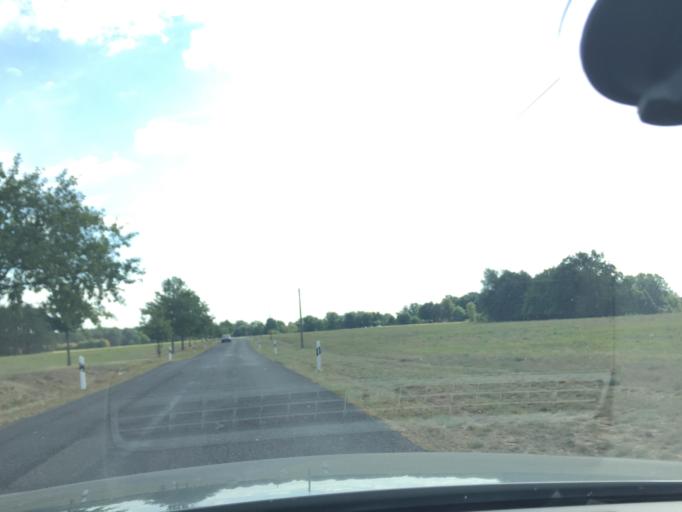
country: DE
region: Brandenburg
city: Grunheide
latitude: 52.3731
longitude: 13.8009
